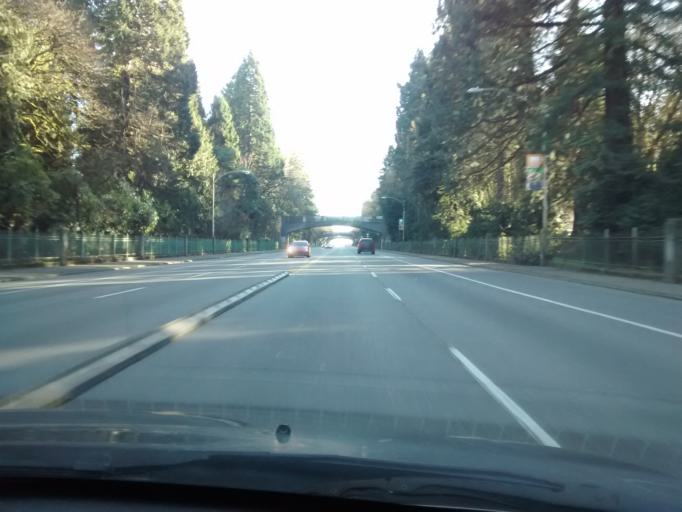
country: US
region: Washington
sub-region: King County
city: Seattle
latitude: 47.6713
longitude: -122.3472
